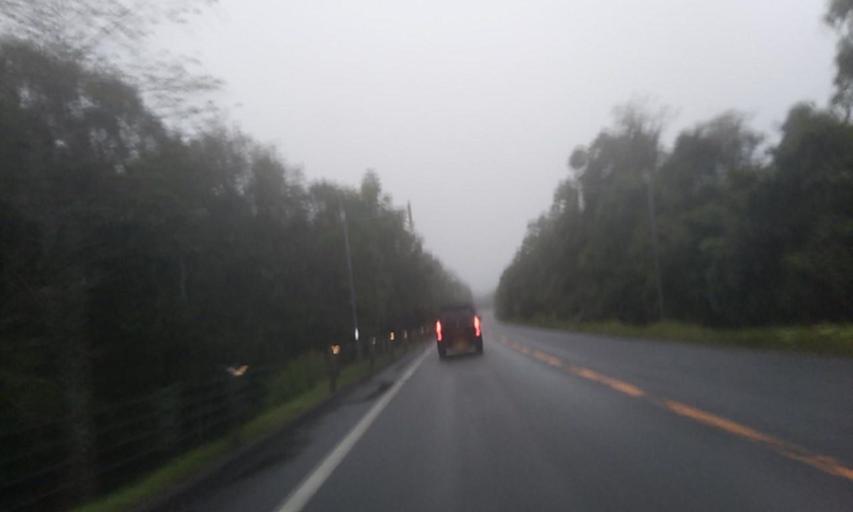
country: JP
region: Hokkaido
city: Kushiro
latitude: 42.9867
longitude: 144.5229
